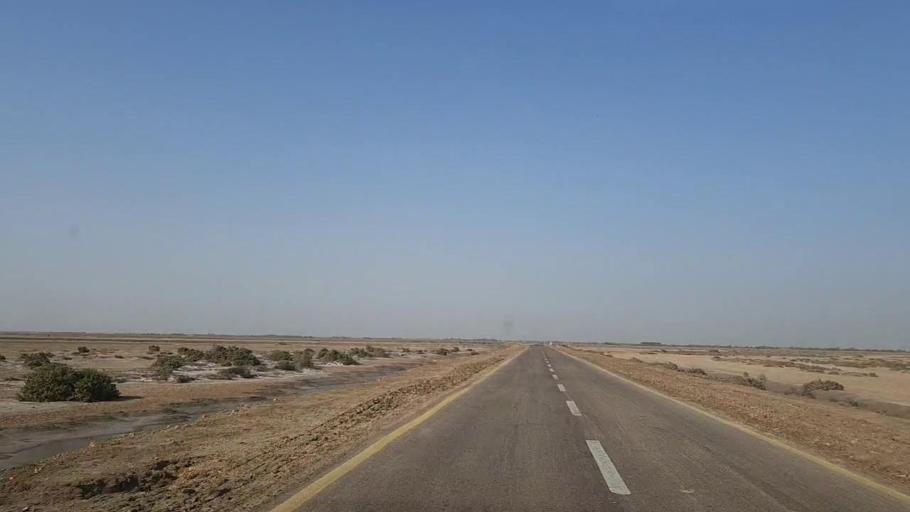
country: PK
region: Sindh
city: Jati
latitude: 24.4924
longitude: 68.3756
